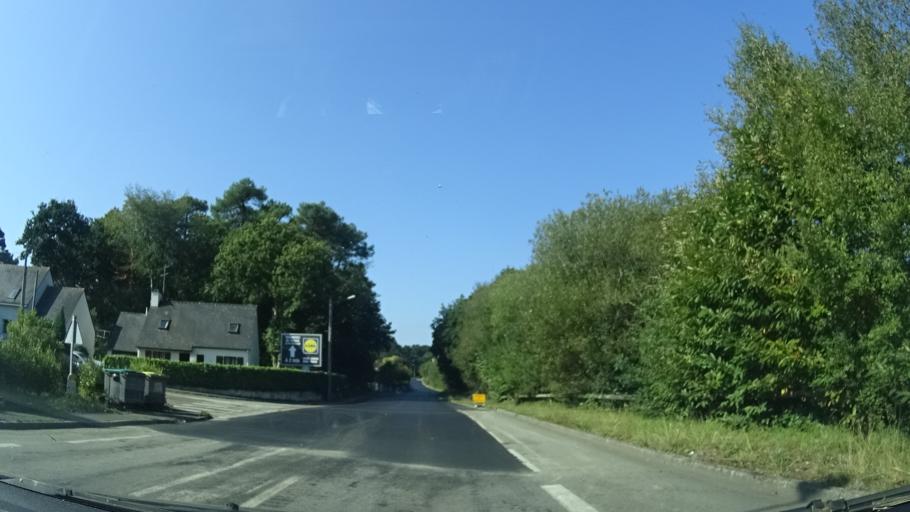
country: FR
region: Brittany
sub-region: Departement du Finistere
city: Douarnenez
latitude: 48.0864
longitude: -4.3362
